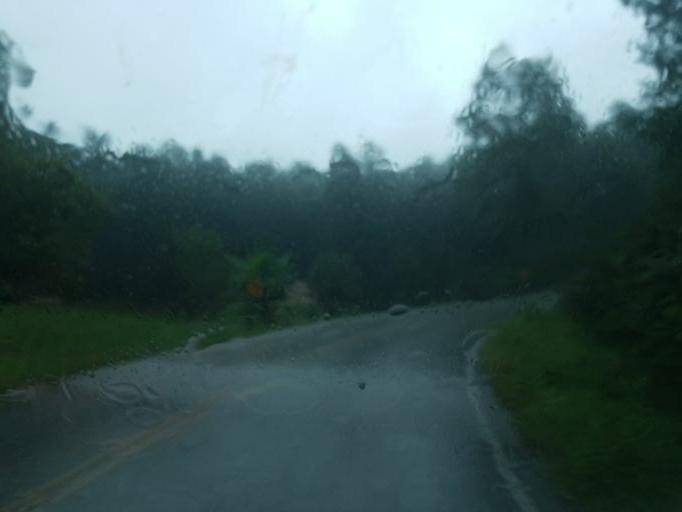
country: US
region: Kentucky
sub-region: Carter County
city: Olive Hill
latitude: 38.3423
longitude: -83.2017
